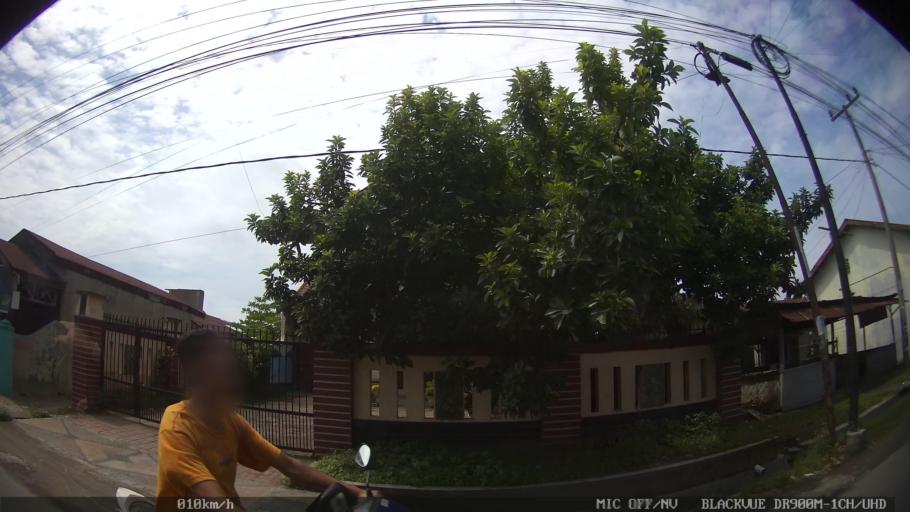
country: ID
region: North Sumatra
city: Medan
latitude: 3.5910
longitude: 98.7437
